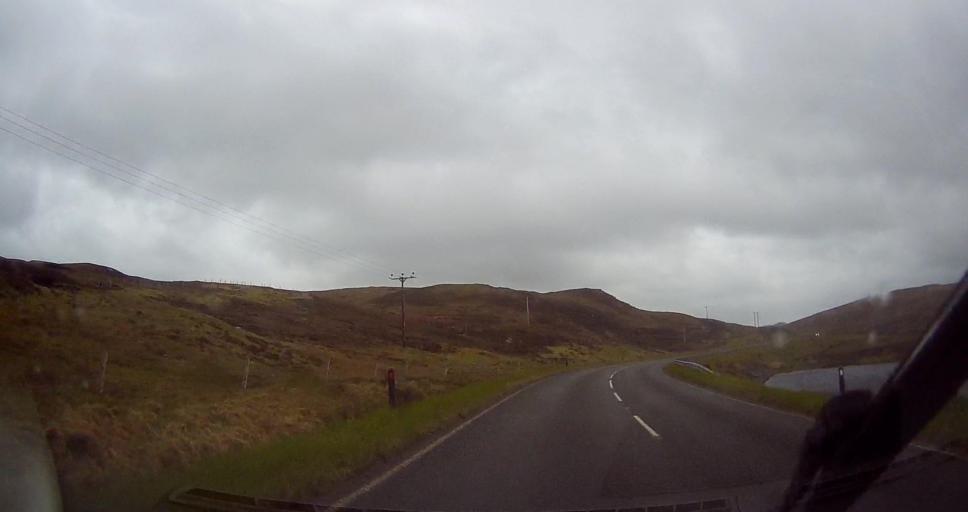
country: GB
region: Scotland
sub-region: Shetland Islands
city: Lerwick
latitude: 60.4431
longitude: -1.3960
